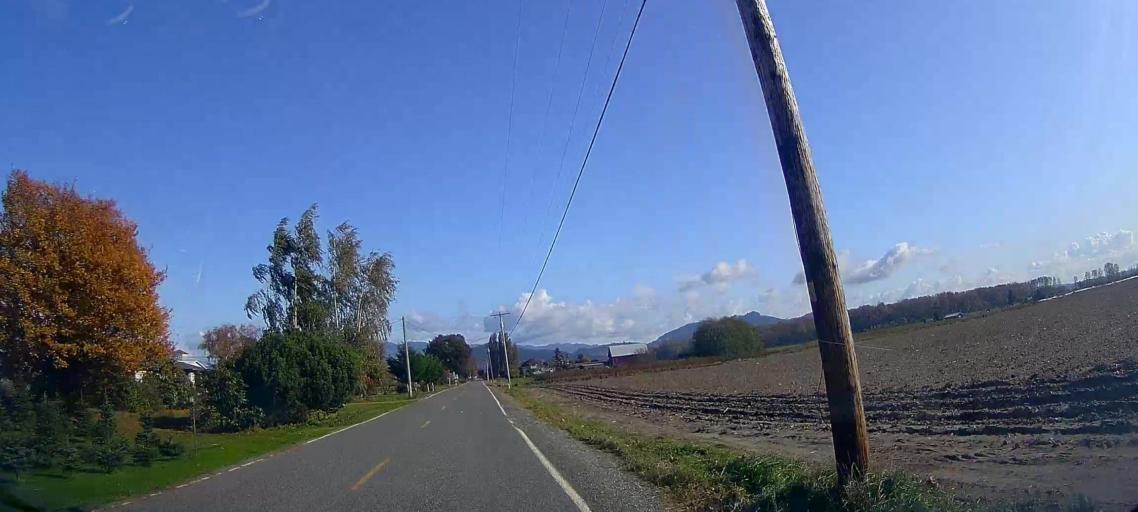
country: US
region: Washington
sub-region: Skagit County
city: Mount Vernon
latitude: 48.3992
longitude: -122.3913
